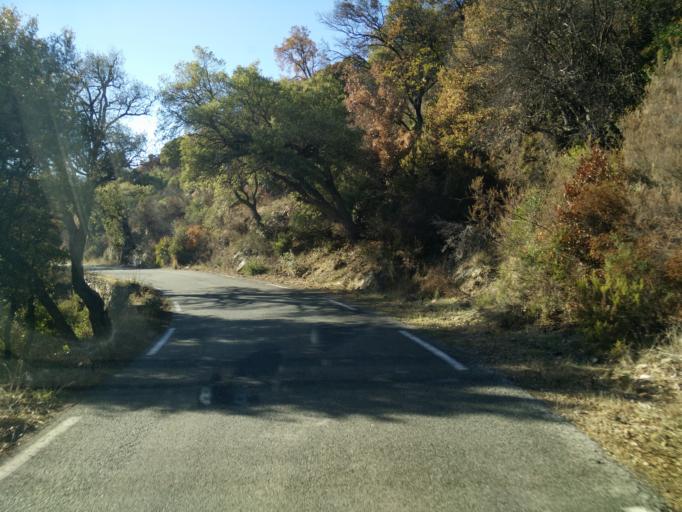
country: FR
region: Provence-Alpes-Cote d'Azur
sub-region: Departement du Var
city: La Garde-Freinet
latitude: 43.2531
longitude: 6.4038
